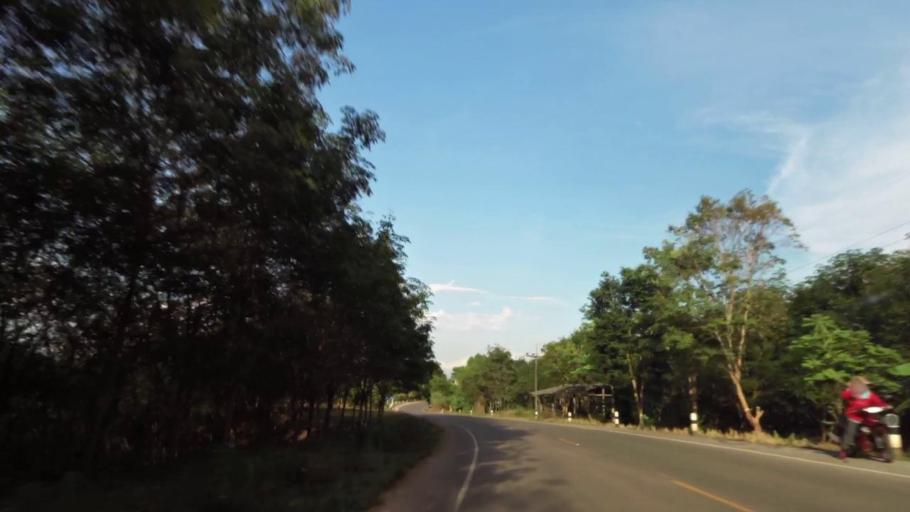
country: TH
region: Chiang Rai
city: Khun Tan
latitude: 19.8552
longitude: 100.3863
